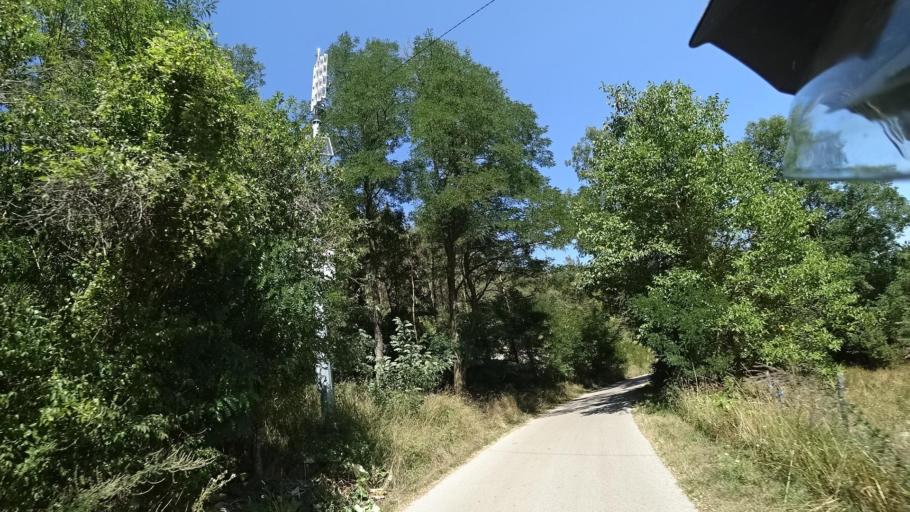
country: HR
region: Licko-Senjska
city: Popovaca
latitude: 44.7080
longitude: 15.2456
